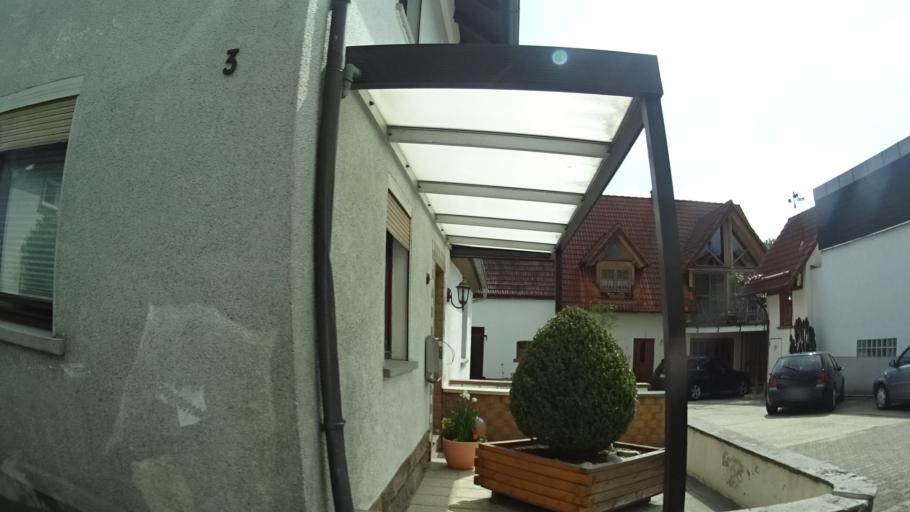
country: DE
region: Bavaria
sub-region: Regierungsbezirk Unterfranken
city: Burkardroth
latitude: 50.2675
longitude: 9.9947
